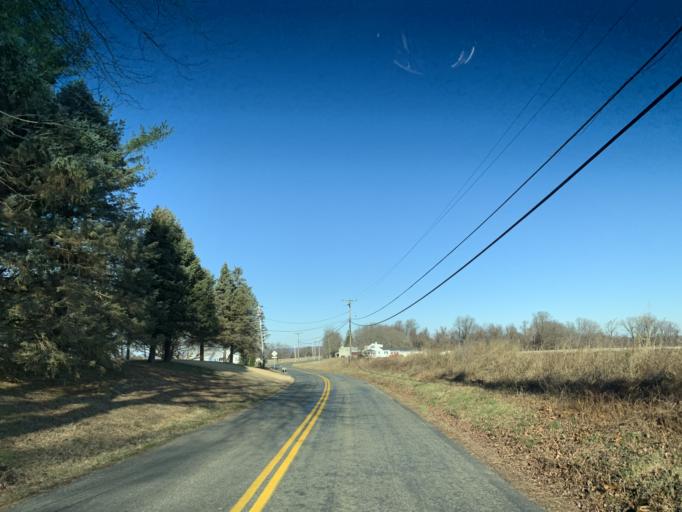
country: US
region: Maryland
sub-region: Harford County
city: Aberdeen
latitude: 39.5825
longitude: -76.1990
